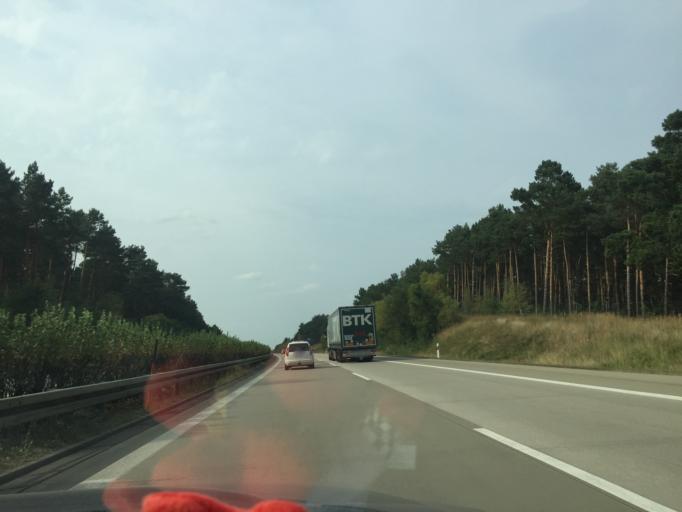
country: DE
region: Brandenburg
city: Schwerin
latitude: 52.1998
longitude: 13.6142
